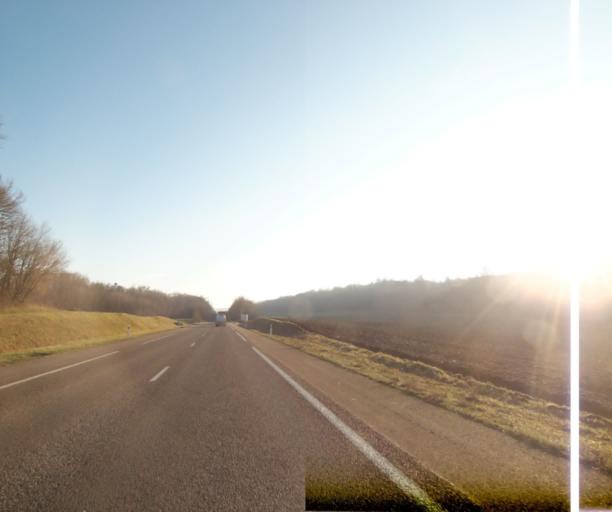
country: FR
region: Champagne-Ardenne
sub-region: Departement de la Haute-Marne
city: Chevillon
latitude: 48.4951
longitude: 5.1102
